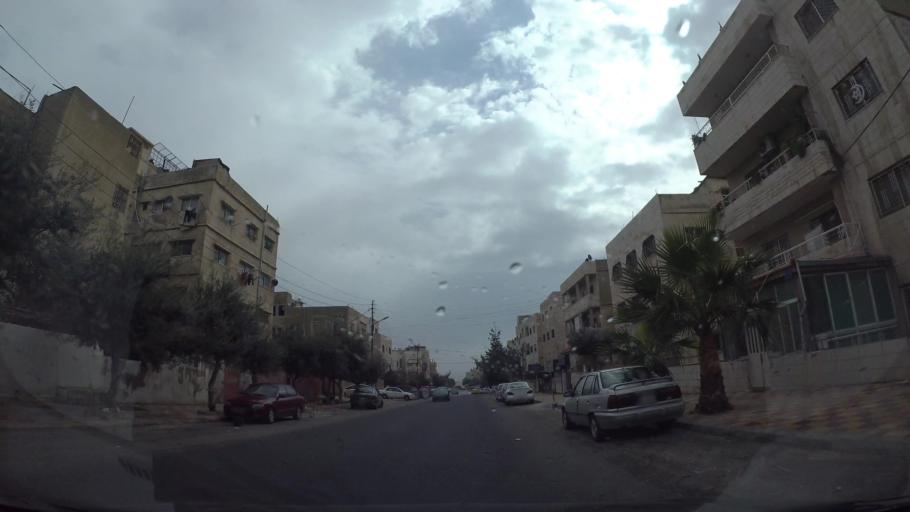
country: JO
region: Amman
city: Amman
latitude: 31.9814
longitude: 35.9261
